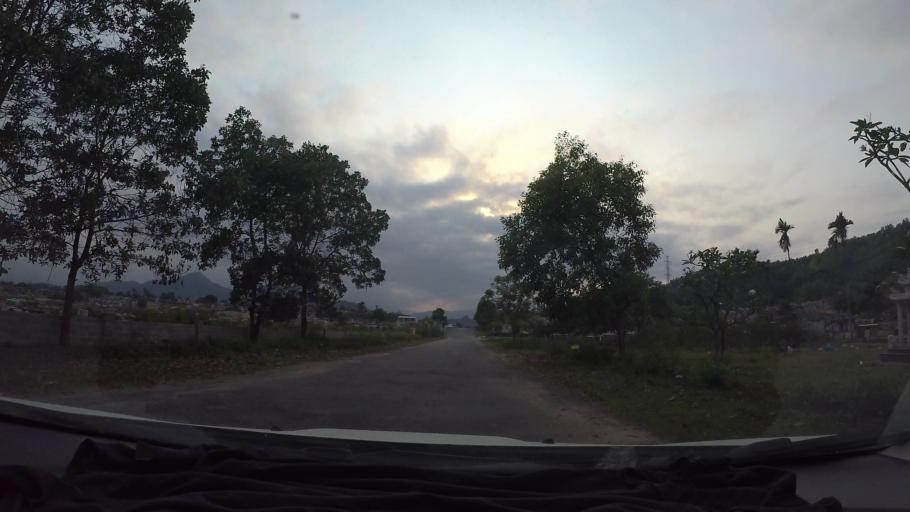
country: VN
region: Da Nang
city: Lien Chieu
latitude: 16.0616
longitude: 108.1096
